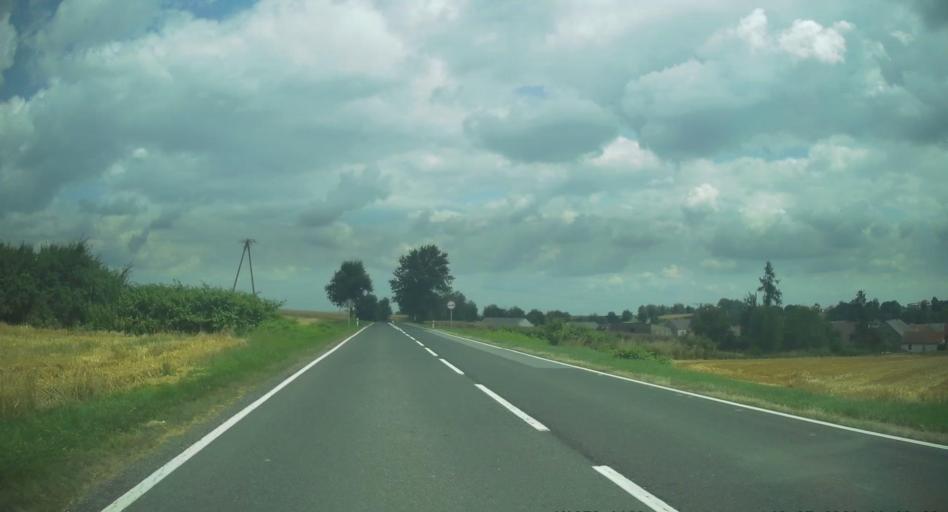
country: PL
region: Opole Voivodeship
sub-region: Powiat prudnicki
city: Raclawice Slaskie
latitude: 50.3446
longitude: 17.7368
